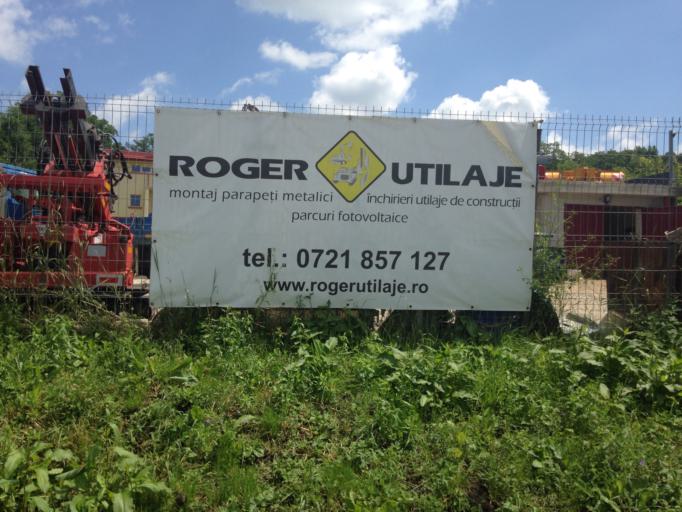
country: RO
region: Cluj
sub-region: Comuna Feleacu
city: Feleacu
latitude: 46.7241
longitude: 23.5794
